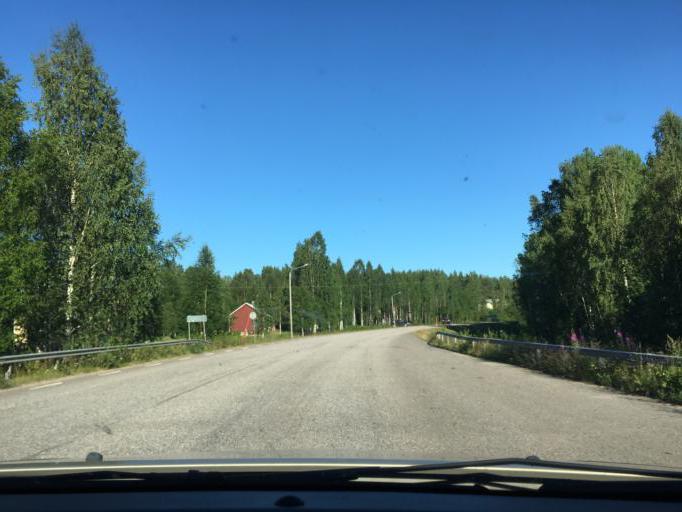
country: SE
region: Norrbotten
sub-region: Kalix Kommun
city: Toere
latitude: 66.0751
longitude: 22.7360
